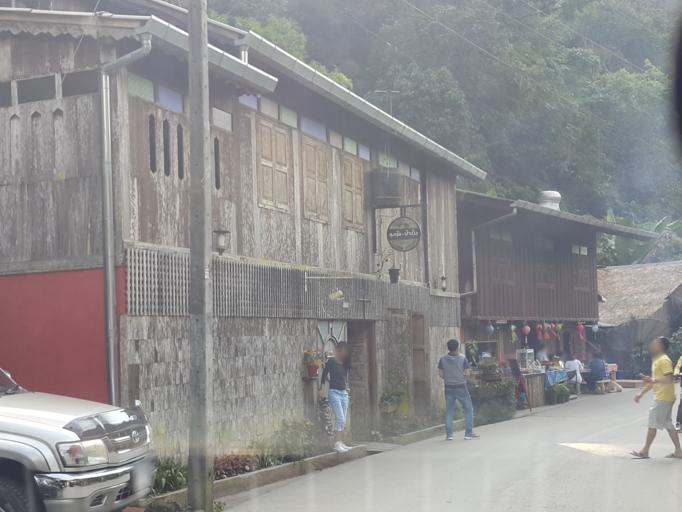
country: TH
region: Chiang Mai
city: Mae On
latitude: 18.8653
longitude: 99.3502
